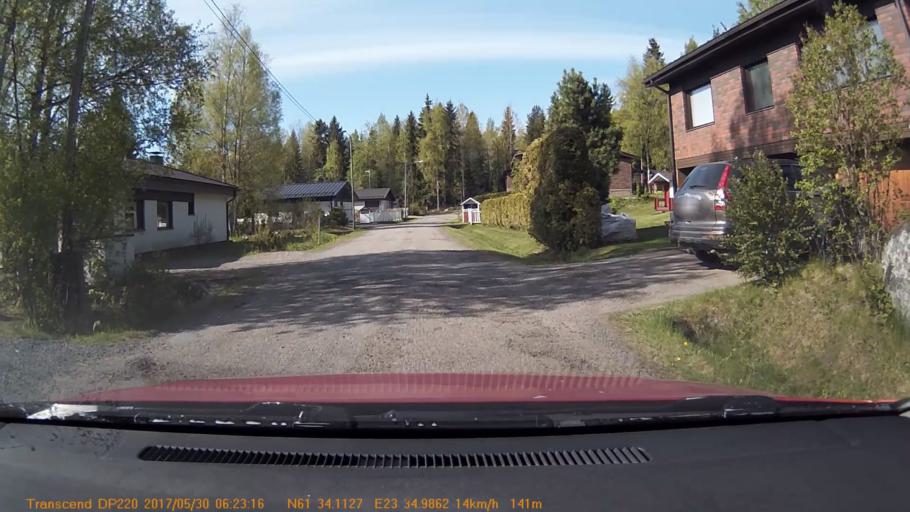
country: FI
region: Pirkanmaa
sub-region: Tampere
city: Yloejaervi
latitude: 61.5686
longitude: 23.5831
